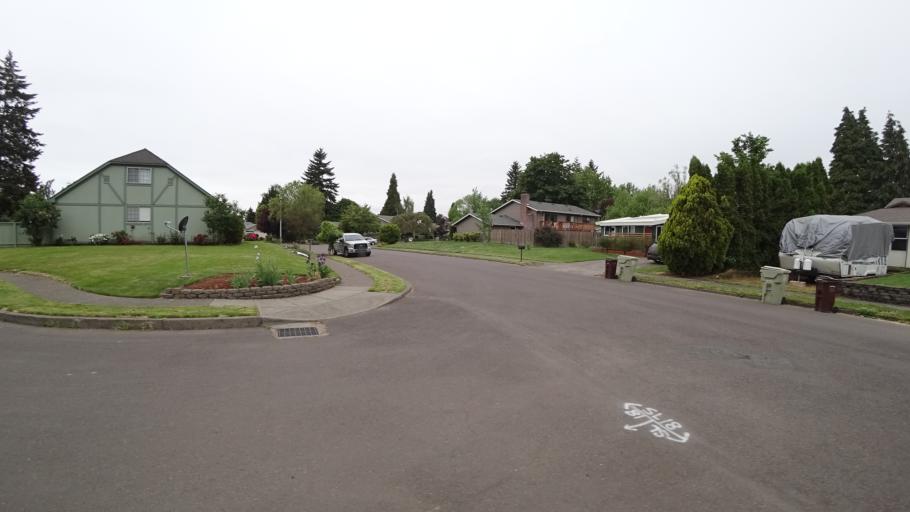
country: US
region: Oregon
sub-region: Washington County
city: Bethany
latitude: 45.5459
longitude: -122.8614
